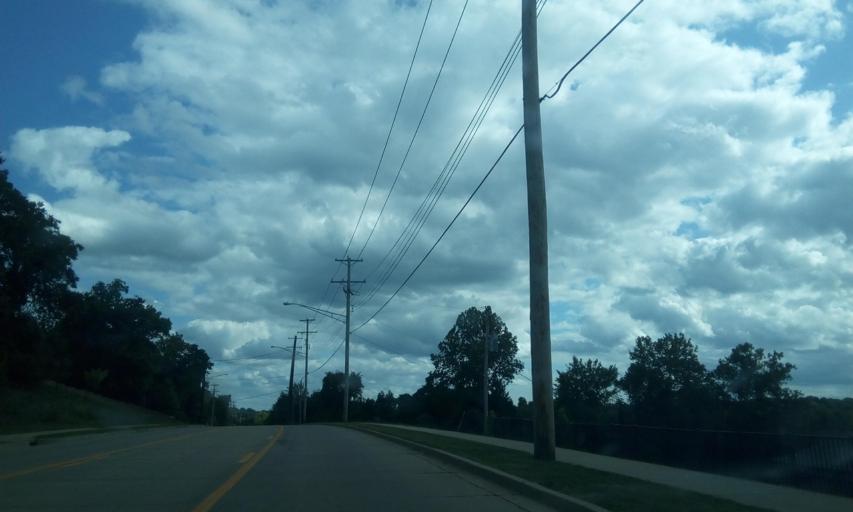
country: US
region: Missouri
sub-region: Saint Louis County
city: Town and Country
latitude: 38.5938
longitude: -90.4729
